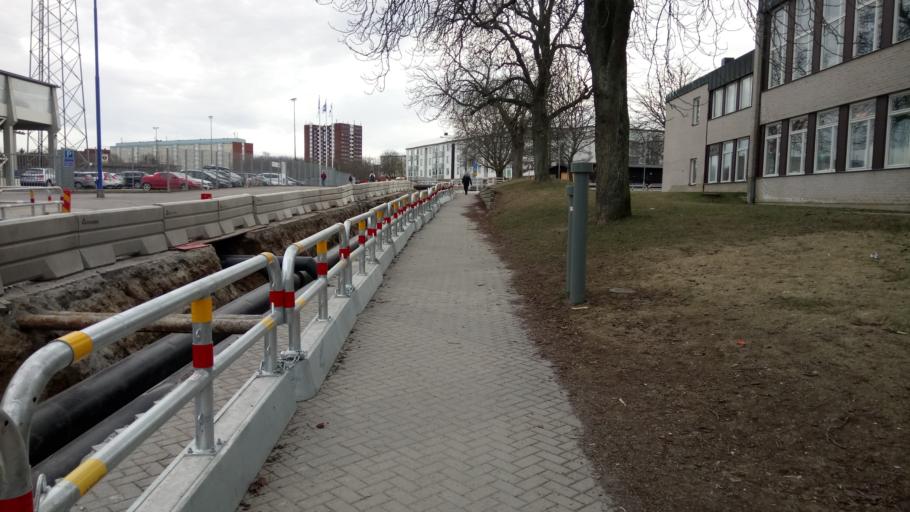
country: SE
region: OEstergoetland
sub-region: Norrkopings Kommun
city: Norrkoping
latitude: 58.5843
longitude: 16.1713
